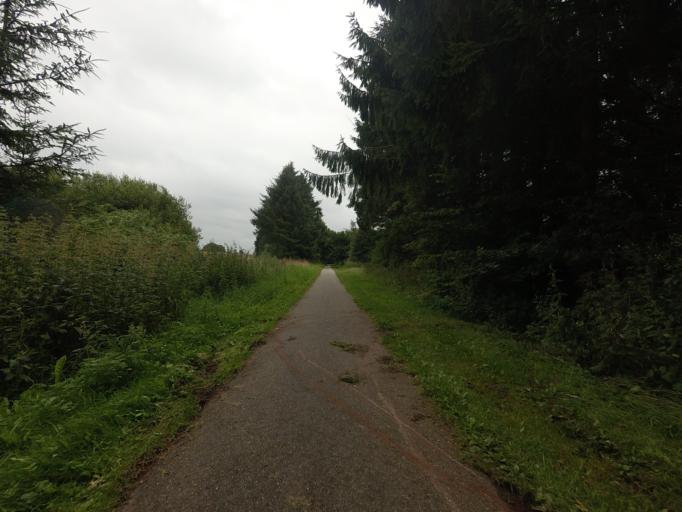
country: DK
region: Central Jutland
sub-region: Horsens Kommune
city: Braedstrup
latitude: 55.9803
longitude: 9.5965
